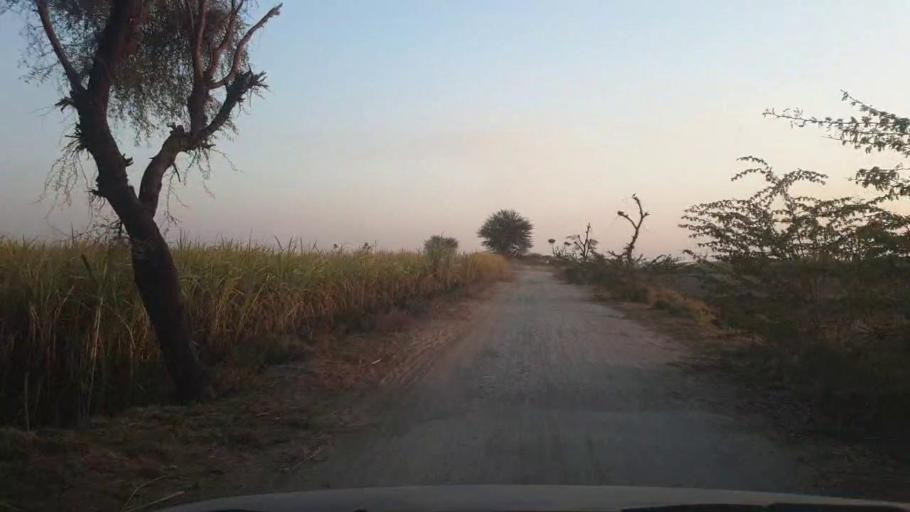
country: PK
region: Sindh
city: Chambar
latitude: 25.2993
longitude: 68.9215
